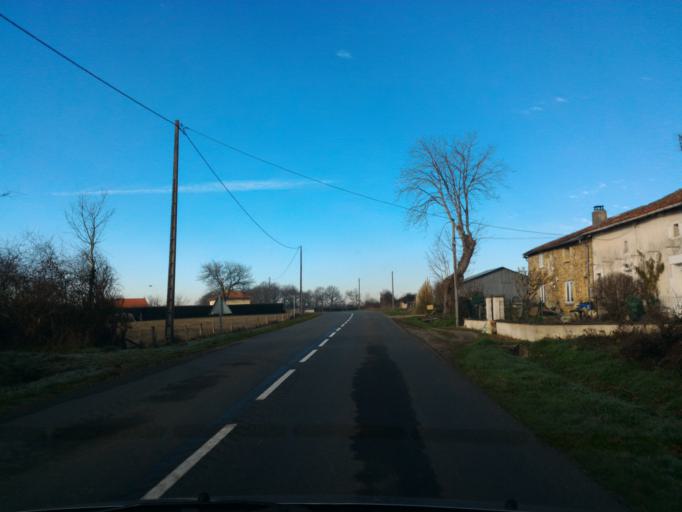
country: FR
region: Poitou-Charentes
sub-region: Departement de la Charente
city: Confolens
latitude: 46.0316
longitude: 0.5514
